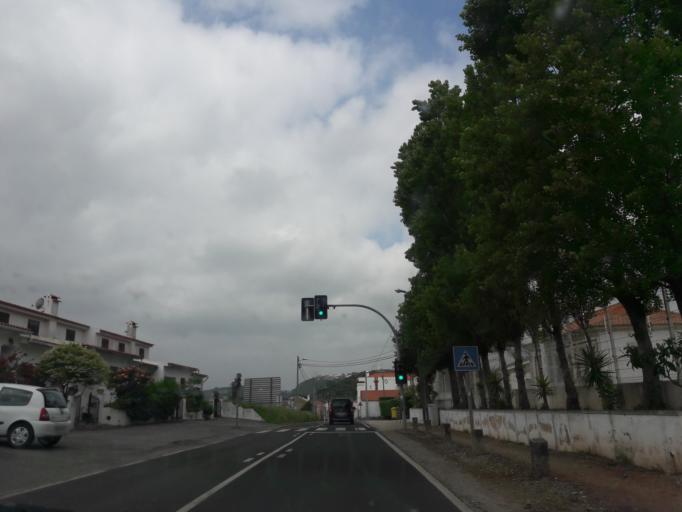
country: PT
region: Leiria
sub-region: Obidos
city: Obidos
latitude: 39.3443
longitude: -9.1687
